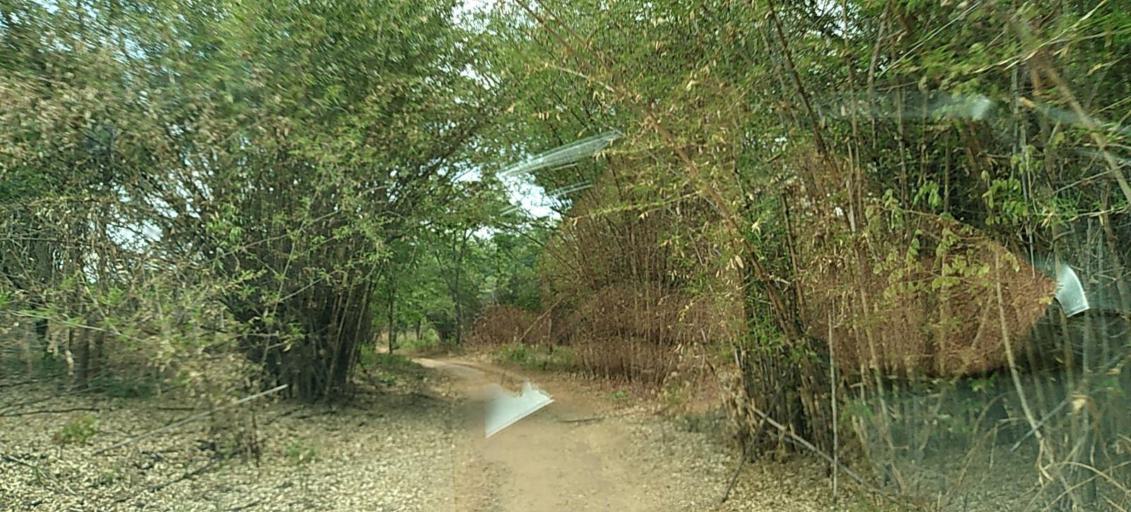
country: ZM
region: Copperbelt
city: Chililabombwe
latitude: -12.4748
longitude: 27.6502
